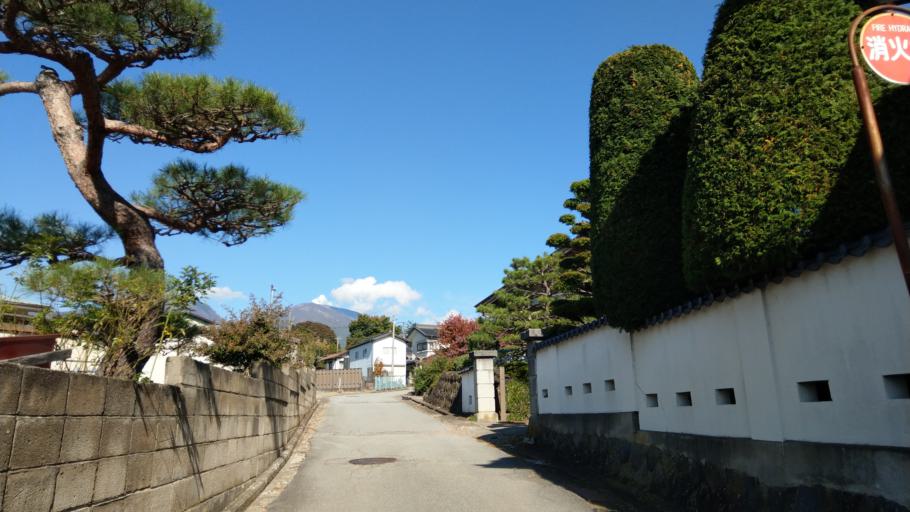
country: JP
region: Nagano
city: Komoro
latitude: 36.3206
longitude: 138.4337
